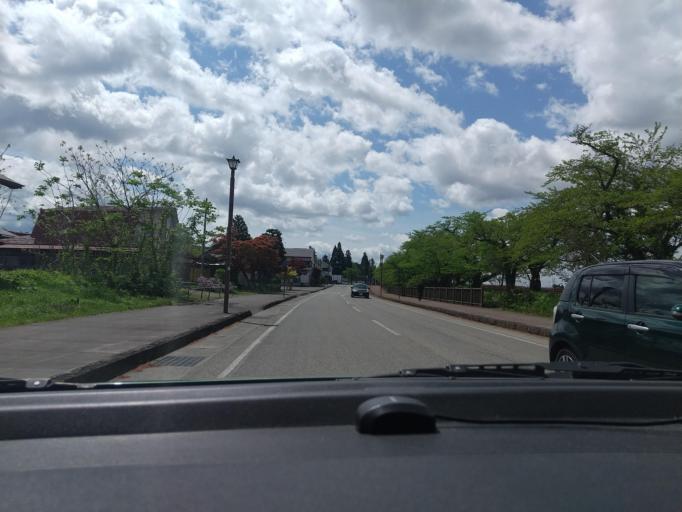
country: JP
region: Akita
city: Kakunodatemachi
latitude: 39.5971
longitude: 140.5607
